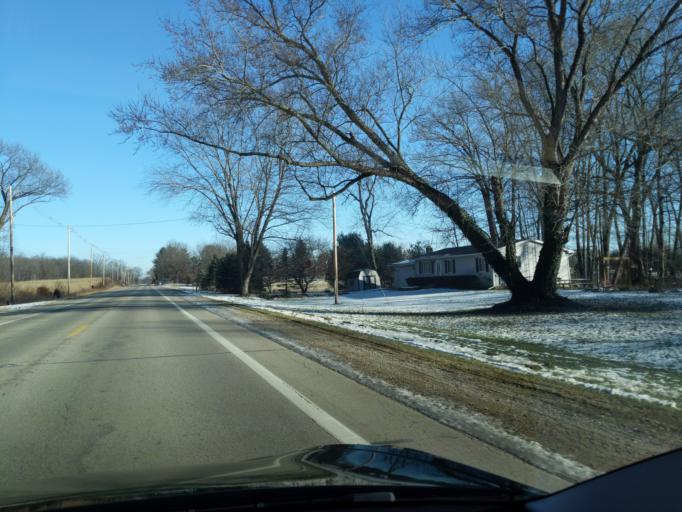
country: US
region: Michigan
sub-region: Ingham County
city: Stockbridge
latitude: 42.3936
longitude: -84.2759
